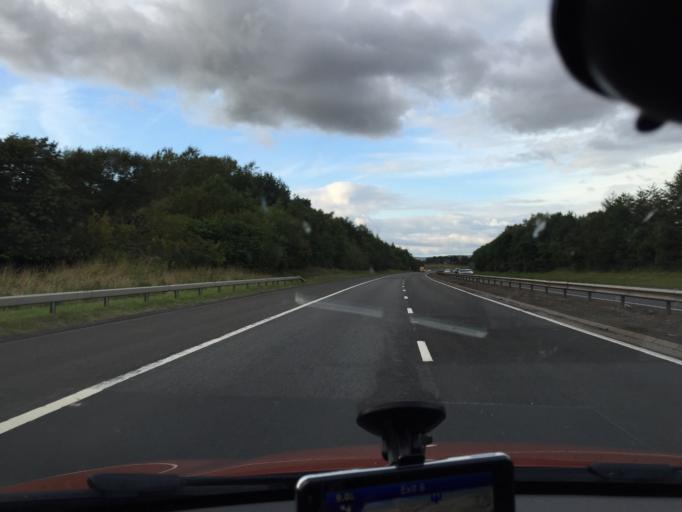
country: GB
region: Scotland
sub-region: North Lanarkshire
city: Glenboig
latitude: 55.9055
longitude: -4.0677
